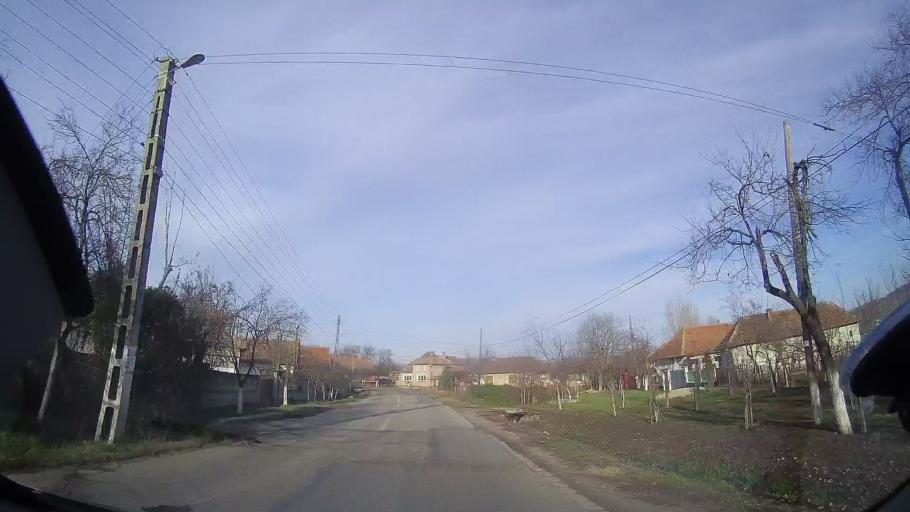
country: RO
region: Bihor
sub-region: Comuna Spinus
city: Spinus
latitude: 47.1766
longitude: 22.2182
